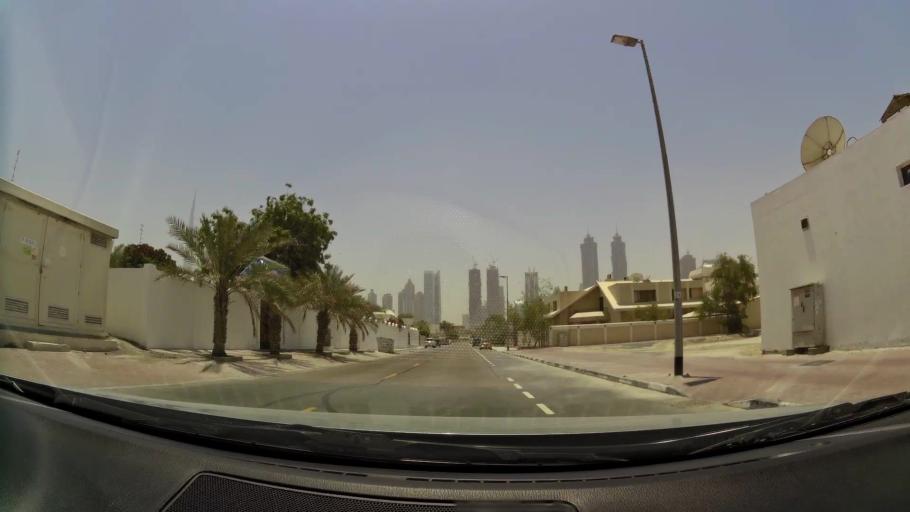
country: AE
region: Dubai
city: Dubai
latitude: 25.1955
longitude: 55.2491
